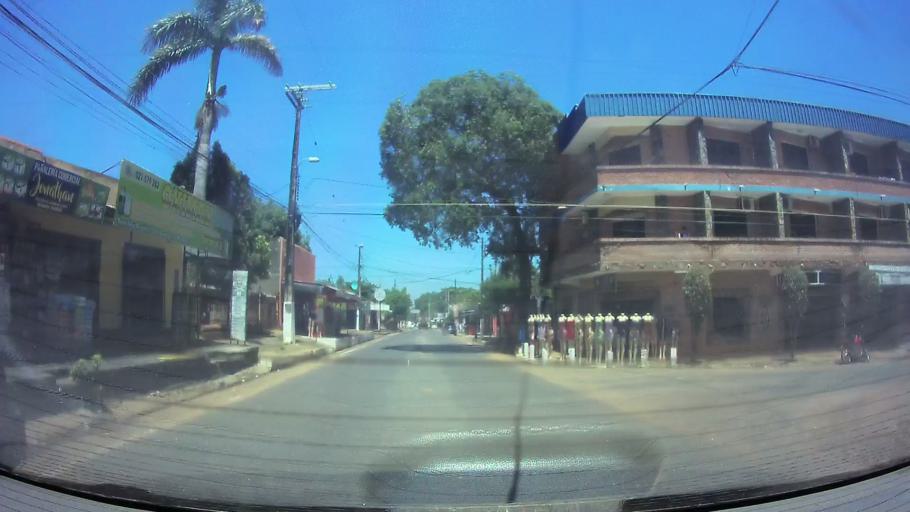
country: PY
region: Central
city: San Lorenzo
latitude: -25.3332
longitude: -57.4869
